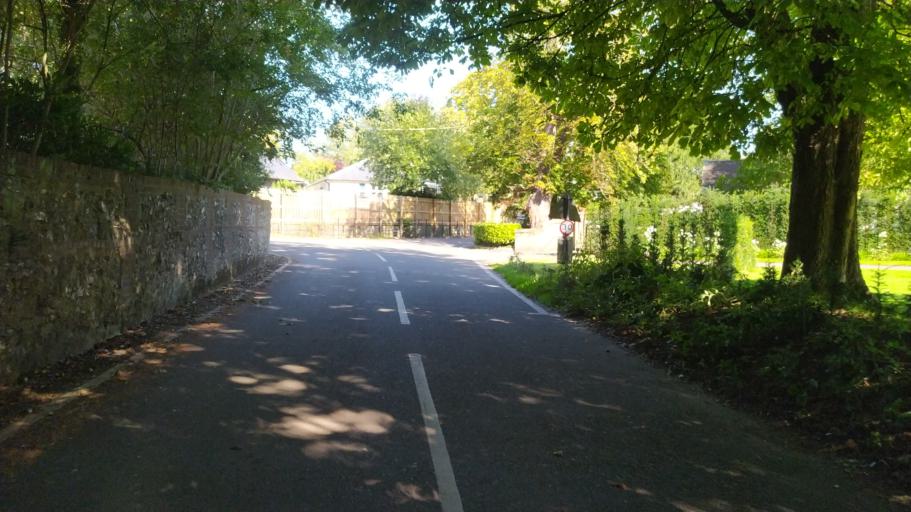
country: GB
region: England
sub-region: Hampshire
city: Abbotts Ann
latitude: 51.1749
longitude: -1.6044
